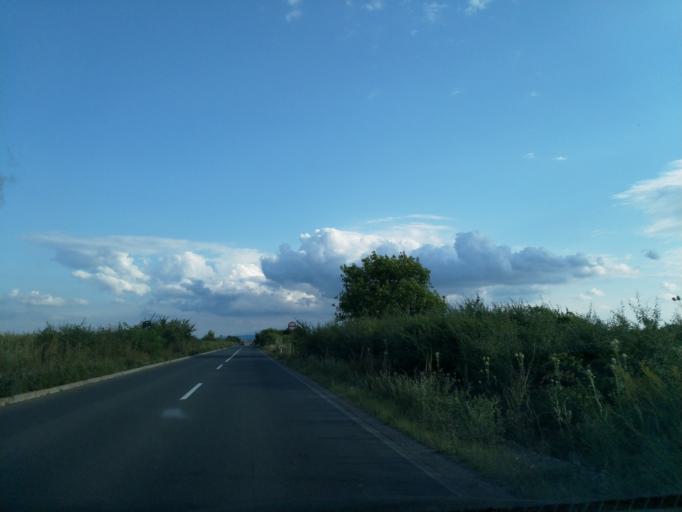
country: RS
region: Central Serbia
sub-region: Pomoravski Okrug
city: Paracin
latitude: 43.8196
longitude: 21.4188
